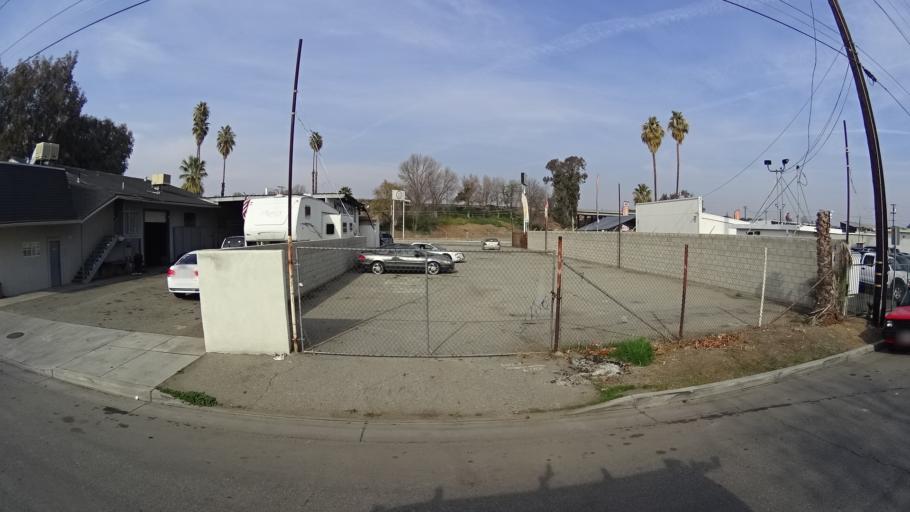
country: US
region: California
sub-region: Kern County
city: Bakersfield
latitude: 35.3810
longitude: -119.0088
